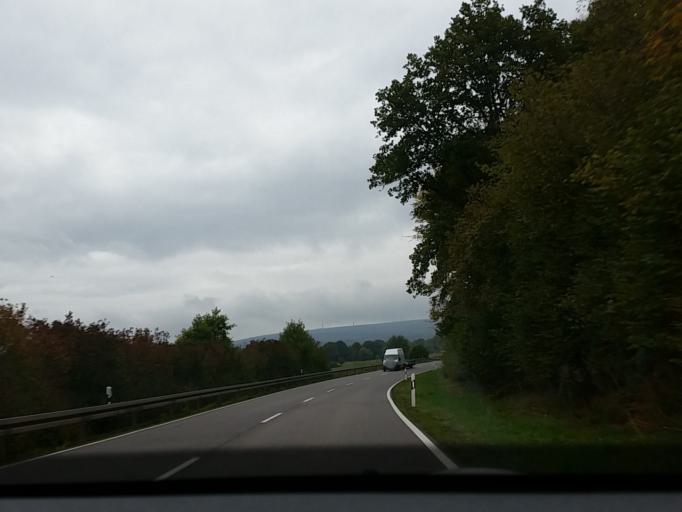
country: DE
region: Saarland
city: Weiskirchen
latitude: 49.5121
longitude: 6.8267
